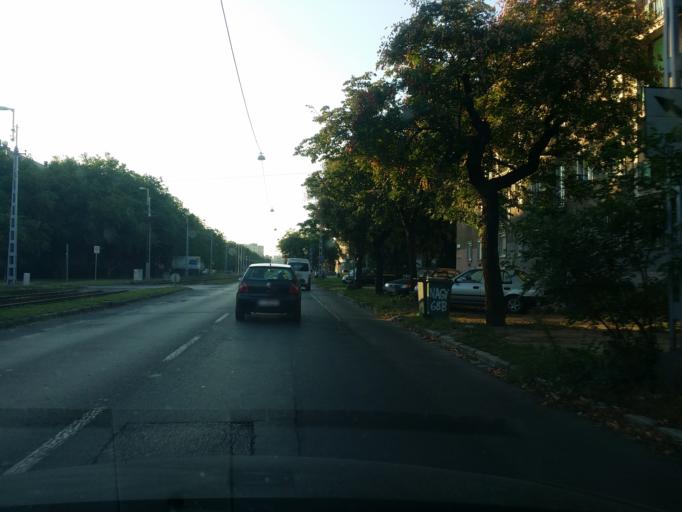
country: HU
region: Budapest
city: Budapest XIV. keruelet
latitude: 47.5107
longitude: 19.1268
